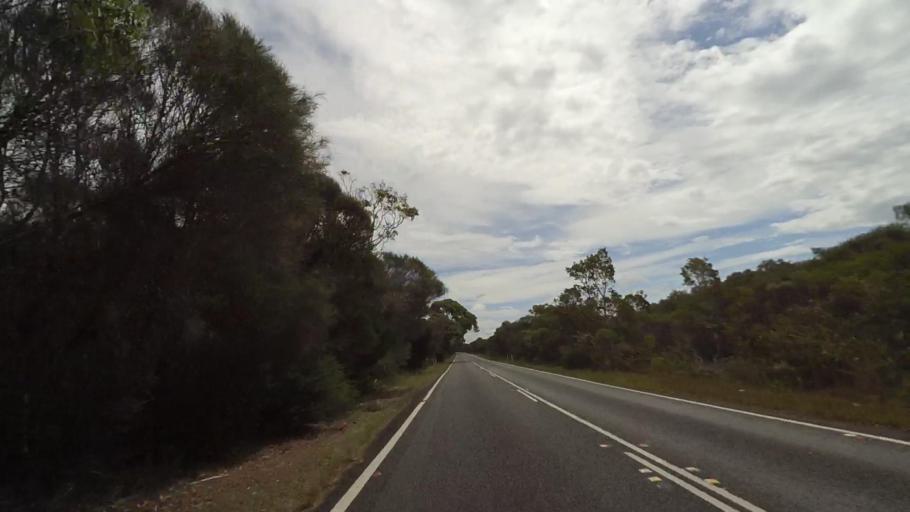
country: AU
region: New South Wales
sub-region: Sutherland Shire
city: Bundeena
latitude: -34.0948
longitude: 151.1314
